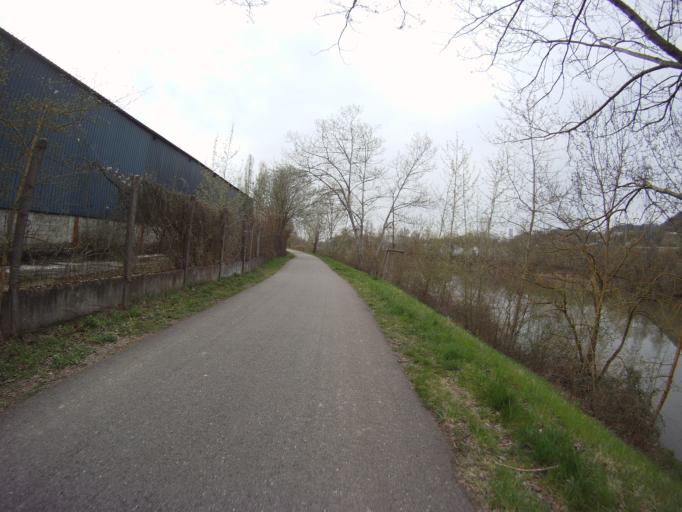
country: FR
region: Lorraine
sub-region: Departement de Meurthe-et-Moselle
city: Malzeville
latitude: 48.7246
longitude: 6.1754
